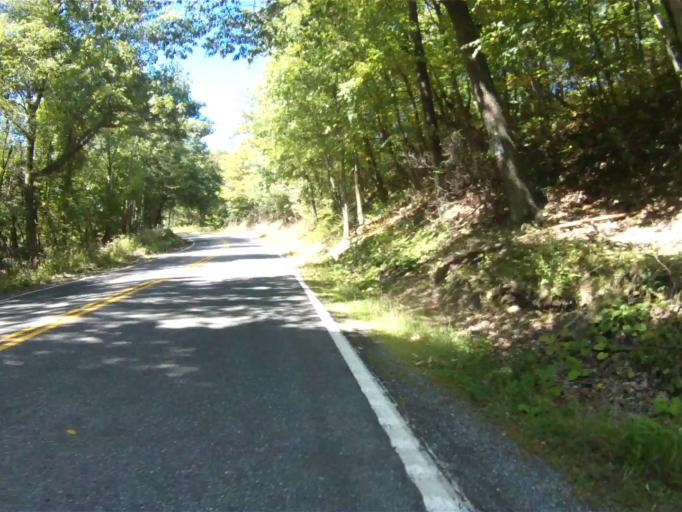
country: US
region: Pennsylvania
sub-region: Centre County
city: Park Forest Village
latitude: 40.9251
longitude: -77.9608
